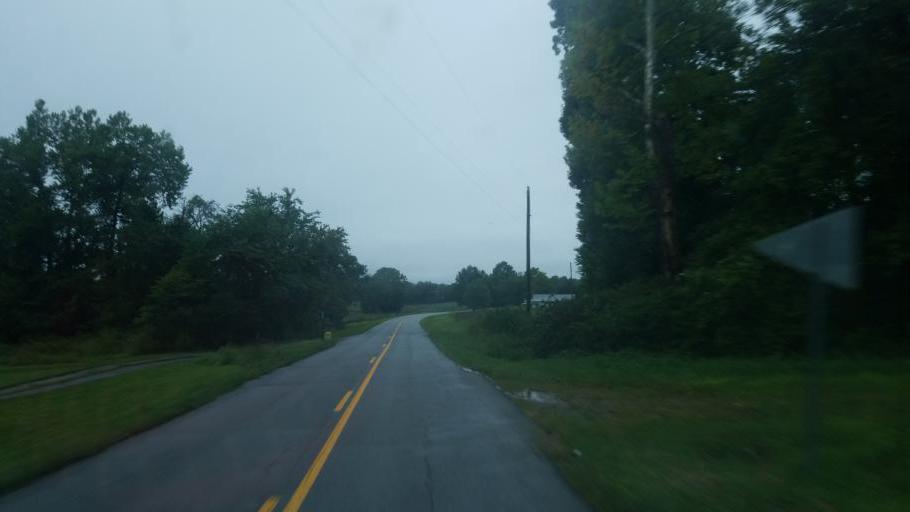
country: US
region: Kentucky
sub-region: Fleming County
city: Flemingsburg
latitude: 38.4048
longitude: -83.5993
